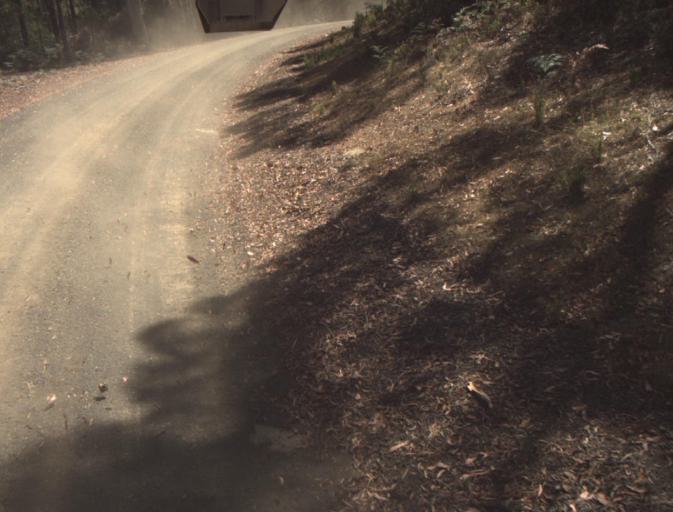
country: AU
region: Tasmania
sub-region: Launceston
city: Newstead
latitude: -41.3025
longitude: 147.3326
